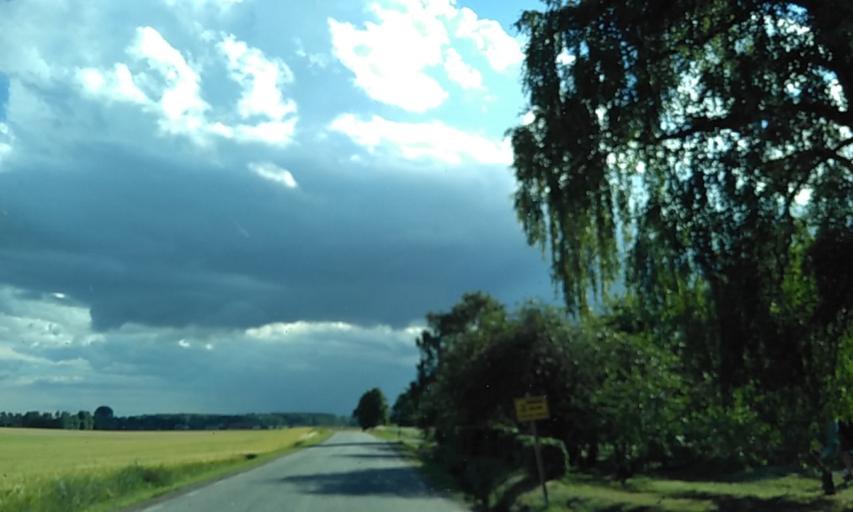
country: SE
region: Vaestra Goetaland
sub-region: Lidkopings Kommun
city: Lidkoping
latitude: 58.5677
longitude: 13.0287
